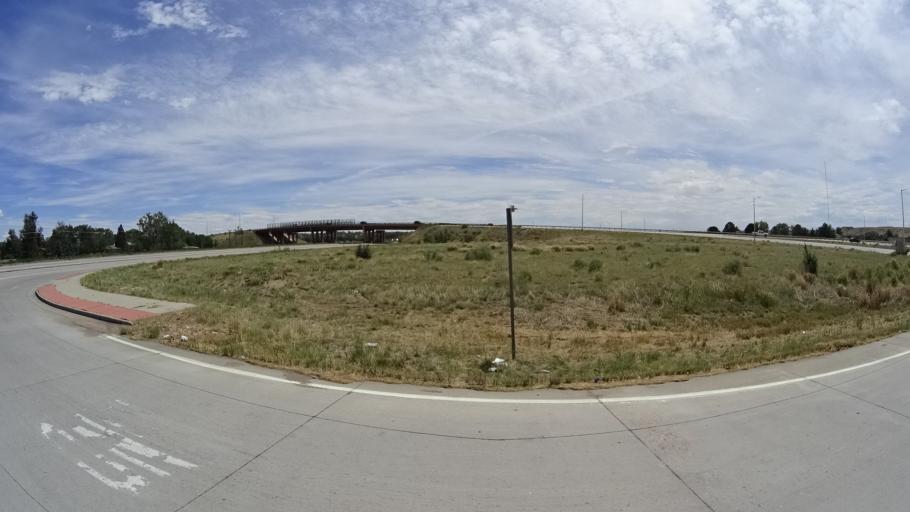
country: US
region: Colorado
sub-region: El Paso County
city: Security-Widefield
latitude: 38.7243
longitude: -104.7204
